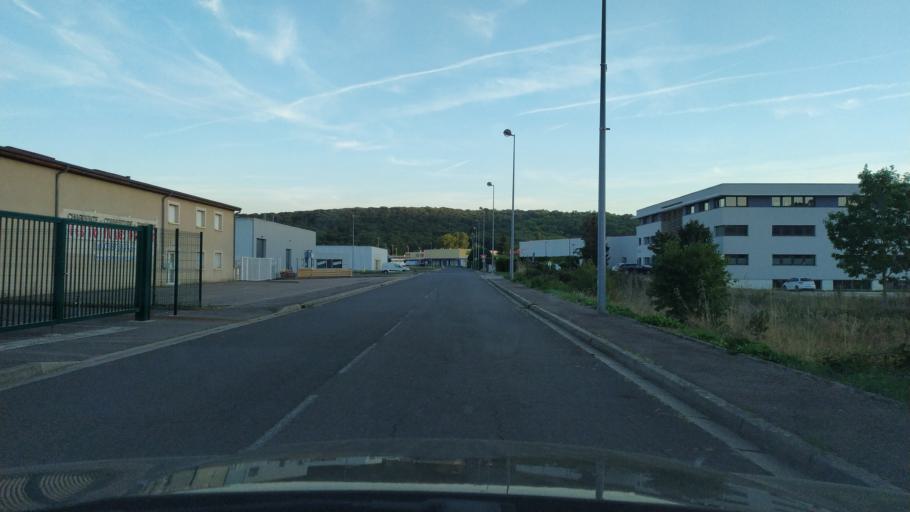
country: FR
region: Lorraine
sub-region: Departement de la Moselle
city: Jouy-aux-Arches
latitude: 49.0791
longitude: 6.0959
